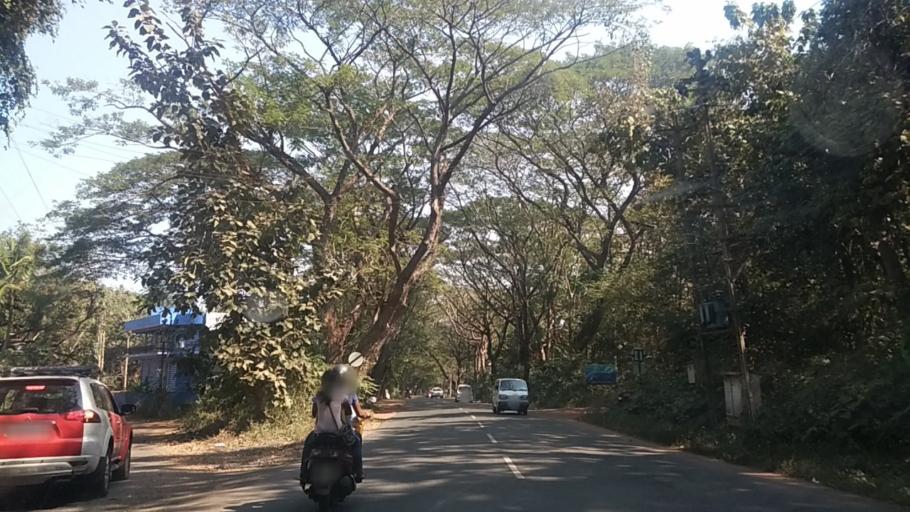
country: IN
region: Goa
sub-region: North Goa
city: Goa Velha
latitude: 15.5002
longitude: 73.8985
